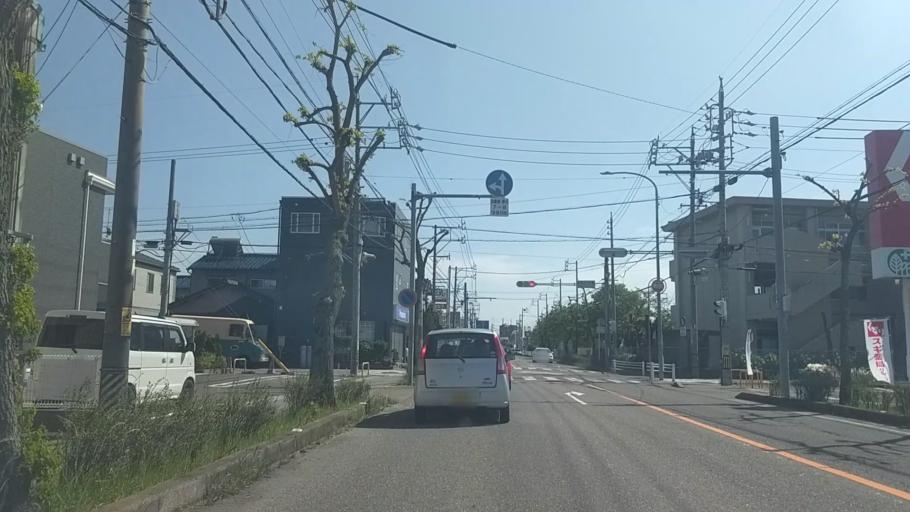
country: JP
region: Aichi
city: Okazaki
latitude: 34.9813
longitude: 137.1388
